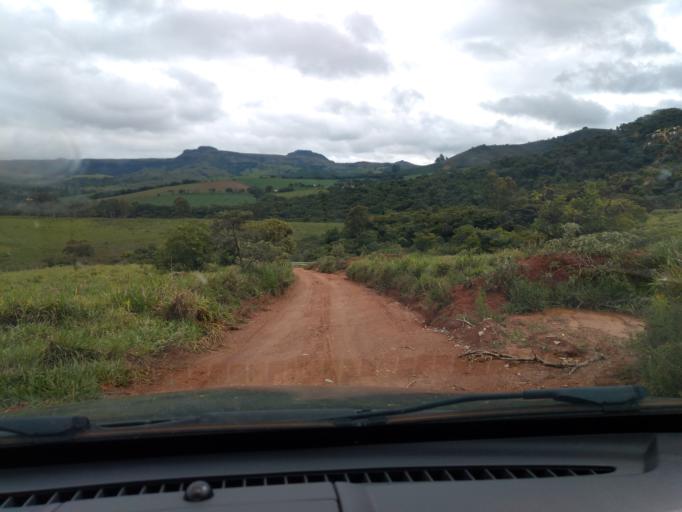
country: BR
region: Minas Gerais
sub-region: Lavras
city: Lavras
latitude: -21.5212
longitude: -44.9301
